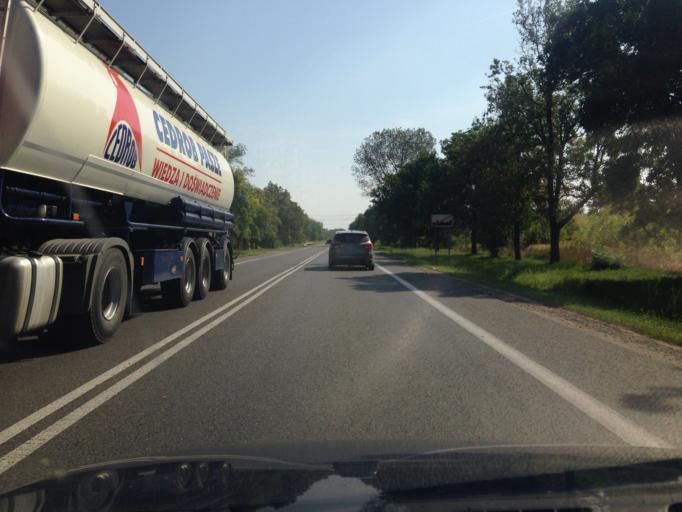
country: PL
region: Masovian Voivodeship
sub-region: Powiat plonski
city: Plonsk
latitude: 52.6109
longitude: 20.3680
